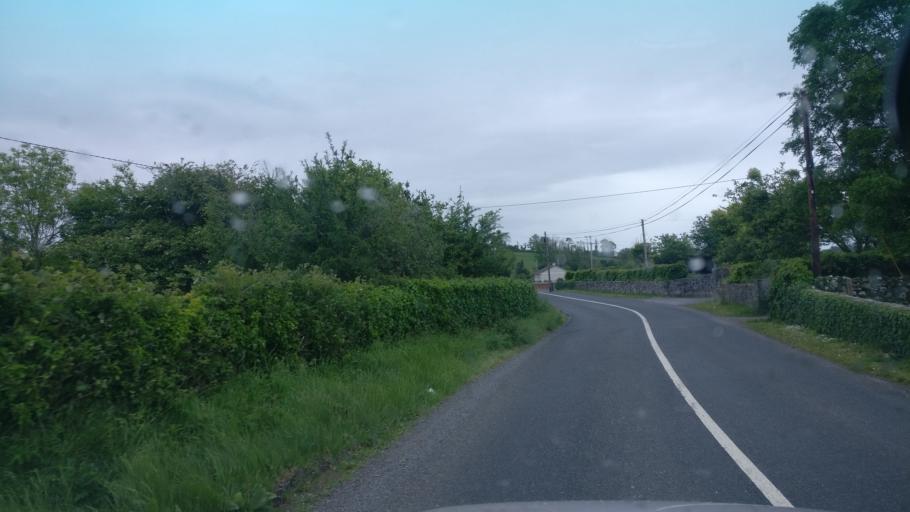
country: IE
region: Connaught
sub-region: County Galway
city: Gort
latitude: 53.0623
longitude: -8.7657
